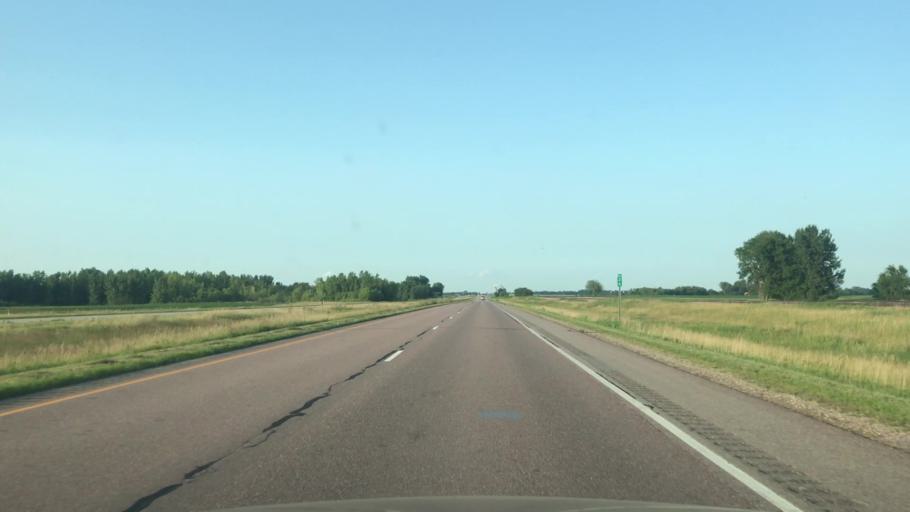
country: US
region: Minnesota
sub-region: Jackson County
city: Lakefield
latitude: 43.7695
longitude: -95.3622
